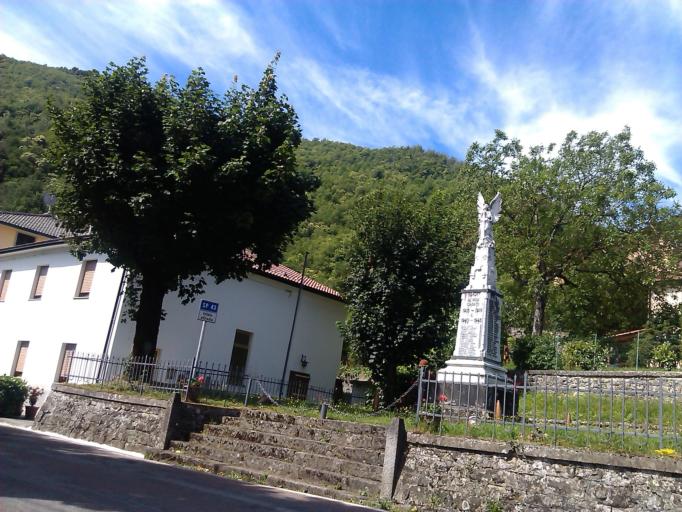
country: IT
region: Tuscany
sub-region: Provincia di Pistoia
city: Sambuca Pistoiese
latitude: 44.1187
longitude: 11.0281
